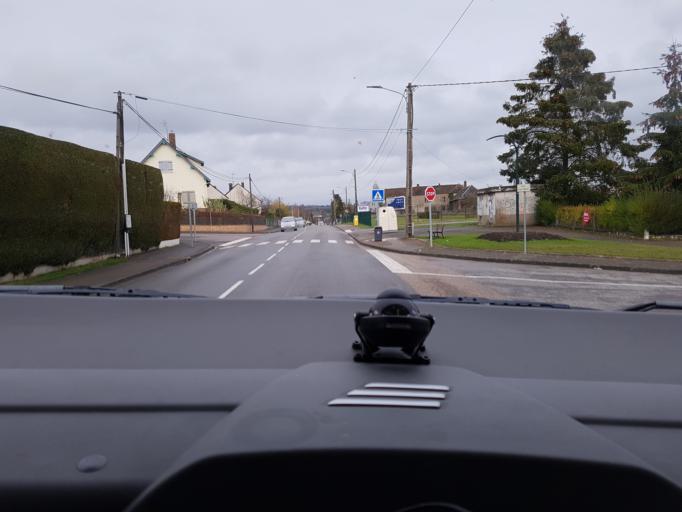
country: FR
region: Haute-Normandie
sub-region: Departement de la Seine-Maritime
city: Gournay-en-Bray
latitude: 49.4769
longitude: 1.7192
